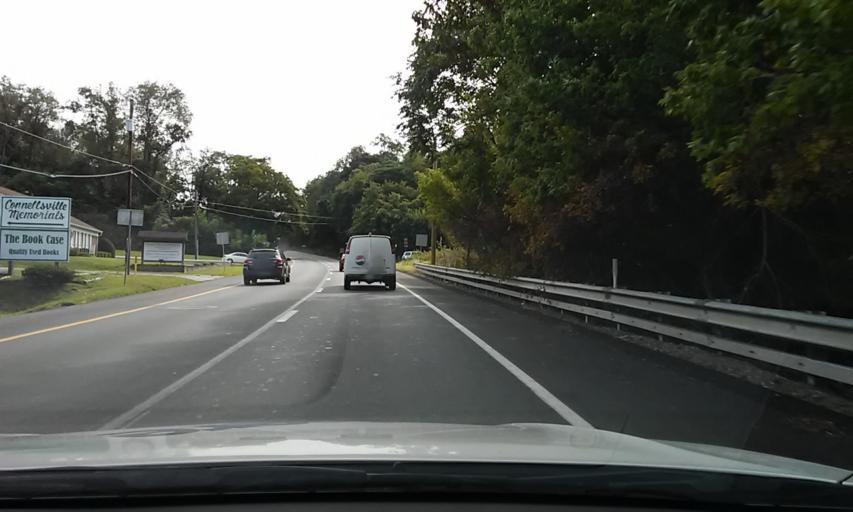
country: US
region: Pennsylvania
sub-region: Fayette County
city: Connellsville
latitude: 40.0091
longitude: -79.6010
